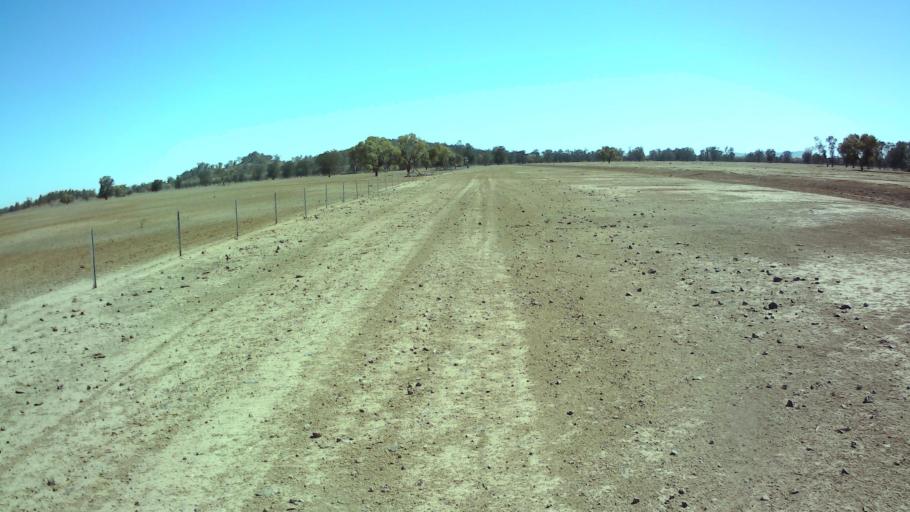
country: AU
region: New South Wales
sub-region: Bland
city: West Wyalong
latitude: -33.7495
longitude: 147.6601
